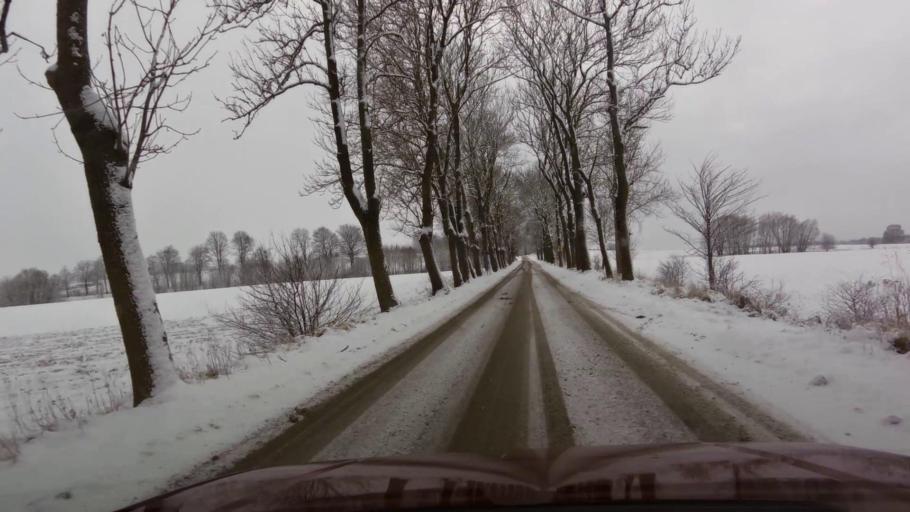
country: PL
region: West Pomeranian Voivodeship
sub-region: Powiat bialogardzki
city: Bialogard
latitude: 53.9840
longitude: 15.9837
